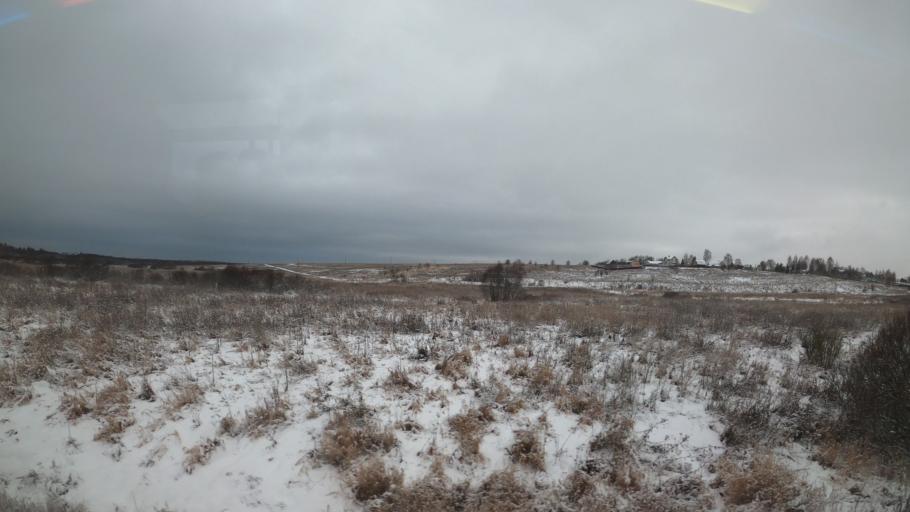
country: RU
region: Jaroslavl
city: Pereslavl'-Zalesskiy
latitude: 56.6991
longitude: 38.9149
